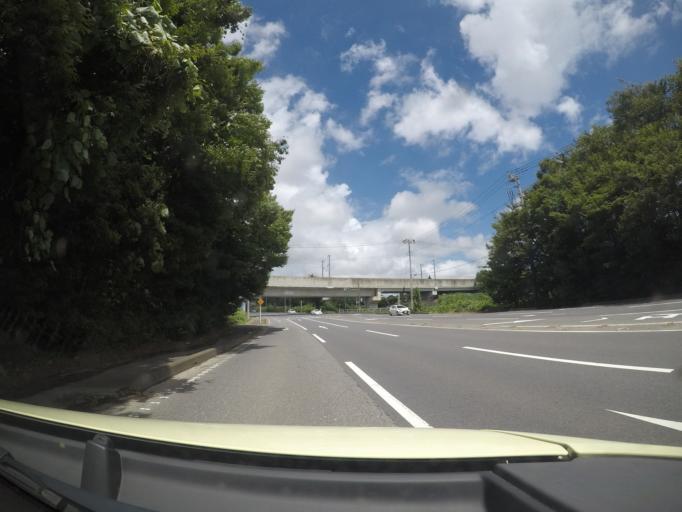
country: JP
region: Ibaraki
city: Naka
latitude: 36.0764
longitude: 140.0676
